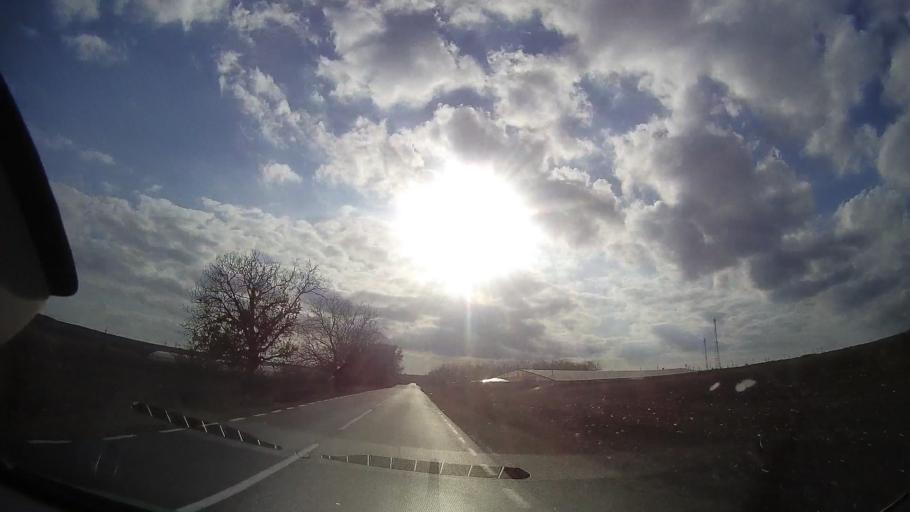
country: RO
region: Constanta
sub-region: Comuna Albesti
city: Albesti
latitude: 43.8115
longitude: 28.4375
